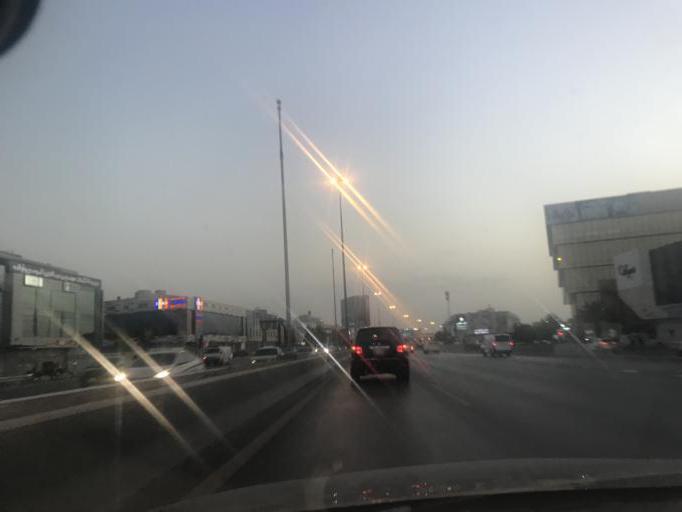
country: SA
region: Ar Riyad
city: Riyadh
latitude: 24.6777
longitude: 46.6860
